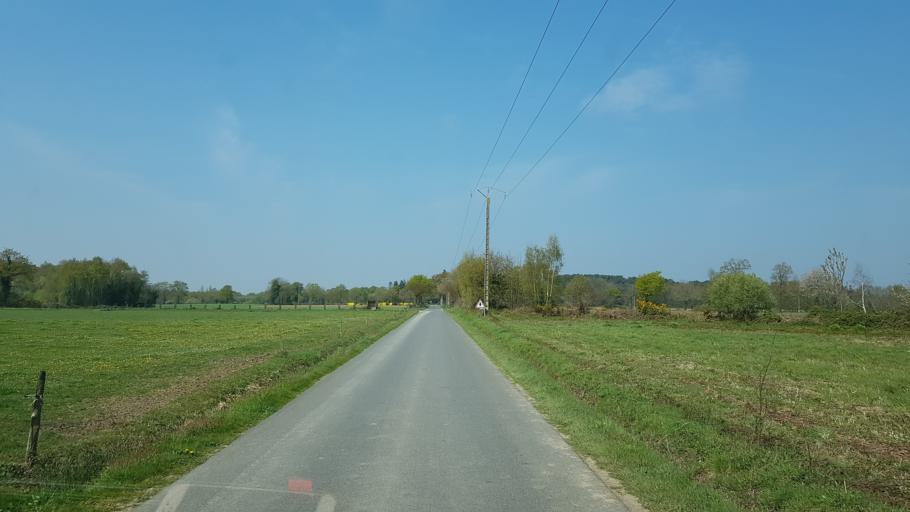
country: FR
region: Brittany
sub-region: Departement du Morbihan
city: Peaule
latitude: 47.5872
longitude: -2.3876
